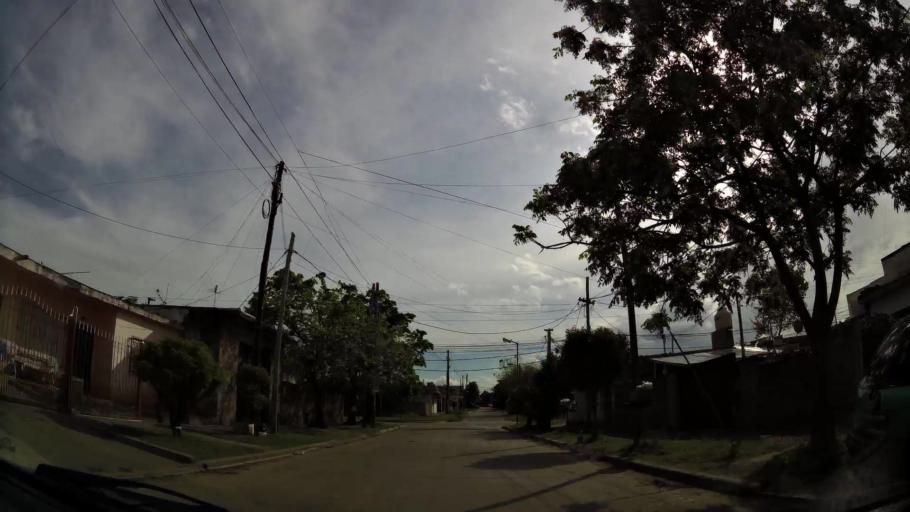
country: AR
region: Buenos Aires
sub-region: Partido de Quilmes
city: Quilmes
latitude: -34.7489
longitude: -58.2748
